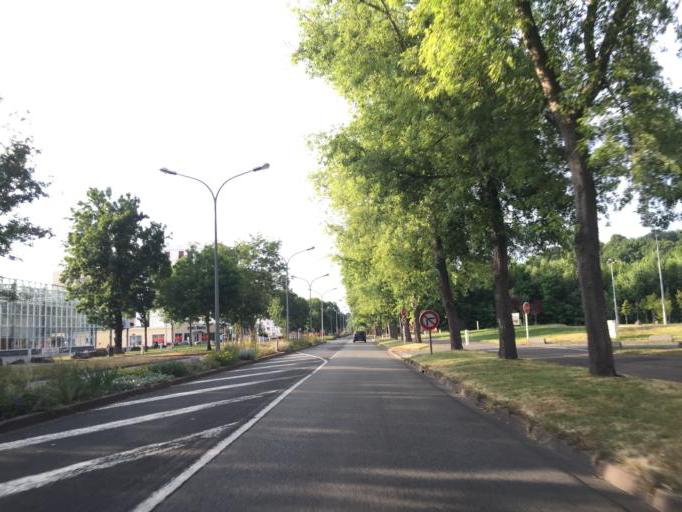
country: FR
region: Auvergne
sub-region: Departement de l'Allier
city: Creuzier-le-Vieux
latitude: 46.1445
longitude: 3.4149
